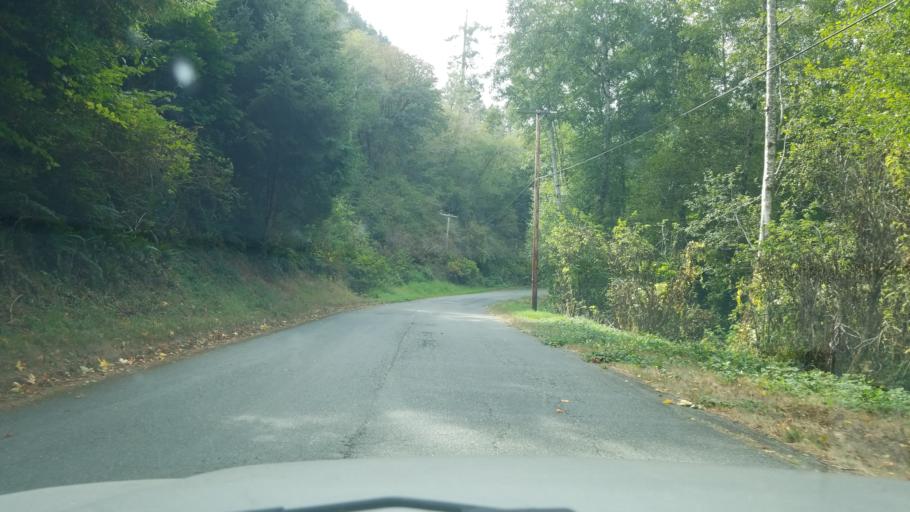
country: US
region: California
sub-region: Del Norte County
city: Bertsch-Oceanview
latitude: 41.5120
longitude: -124.0298
